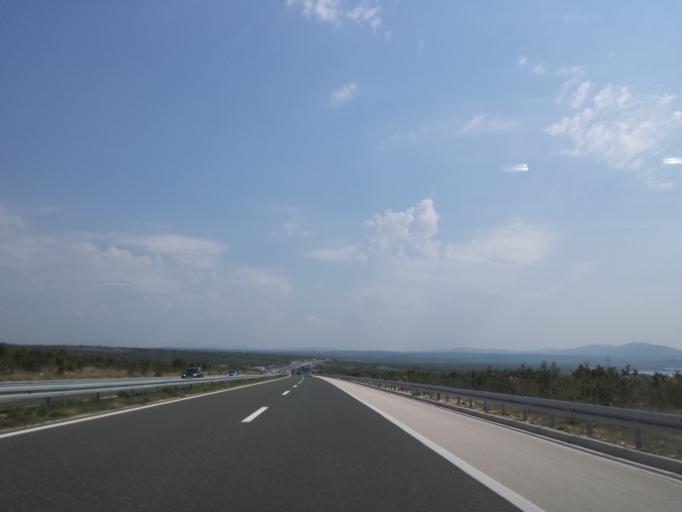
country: HR
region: Sibensko-Kniniska
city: Zaton
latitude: 43.8590
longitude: 15.8329
